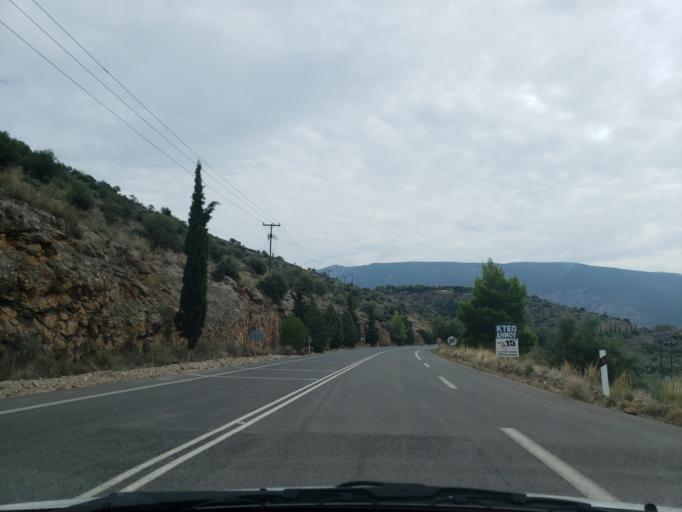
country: GR
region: Central Greece
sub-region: Nomos Fokidos
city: Delphi
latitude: 38.4770
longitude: 22.4531
